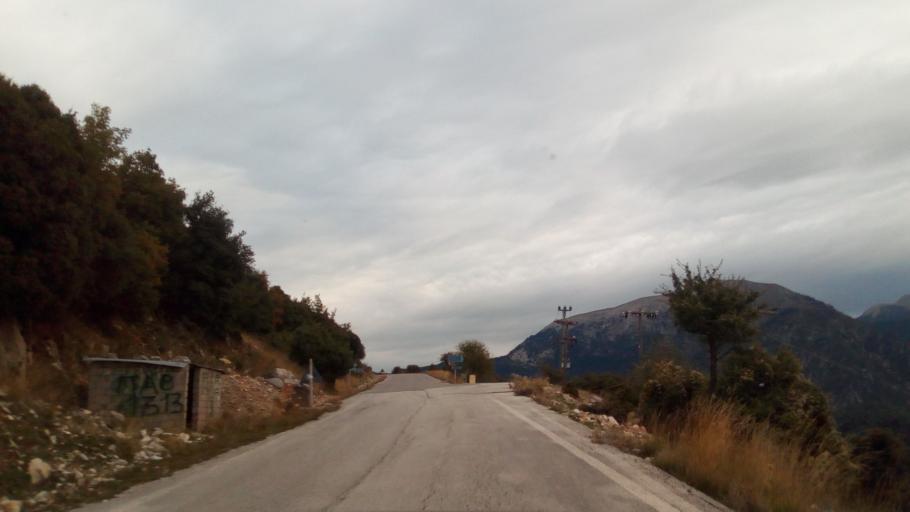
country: GR
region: West Greece
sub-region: Nomos Aitolias kai Akarnanias
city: Thermo
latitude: 38.5929
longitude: 21.8235
